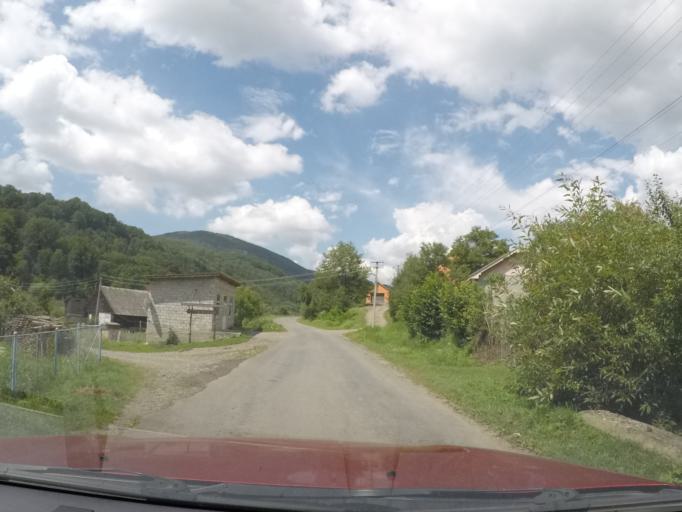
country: UA
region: Zakarpattia
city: Velykyi Bereznyi
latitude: 49.0080
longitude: 22.6368
